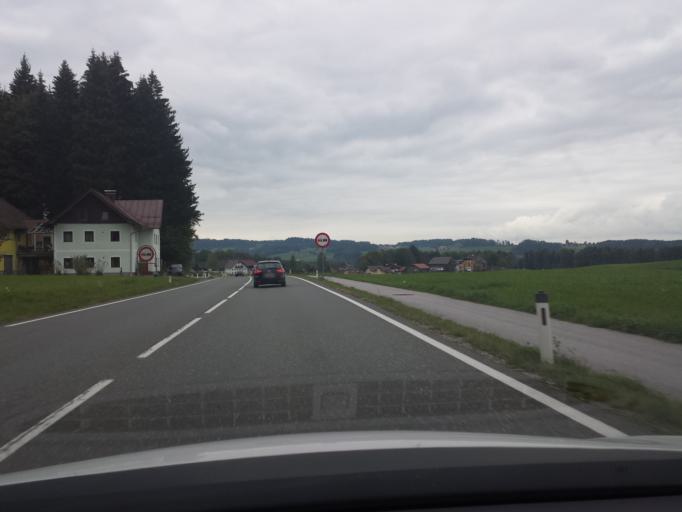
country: AT
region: Salzburg
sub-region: Politischer Bezirk Salzburg-Umgebung
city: Koppl
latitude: 47.8147
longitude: 13.1678
